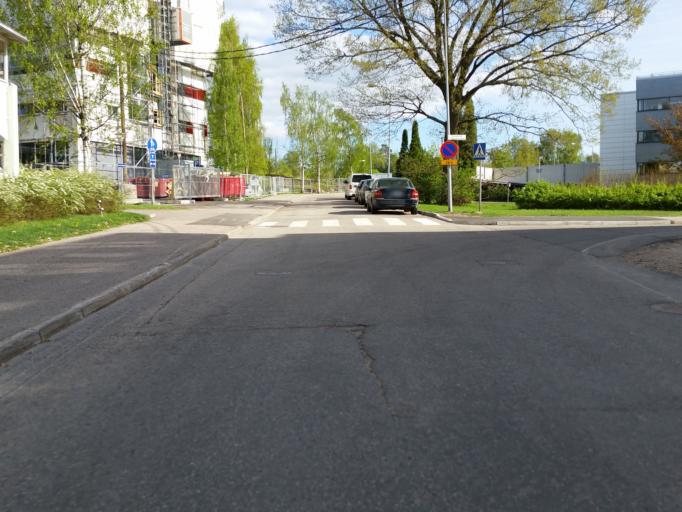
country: FI
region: Uusimaa
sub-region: Helsinki
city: Koukkuniemi
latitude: 60.1695
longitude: 24.7751
